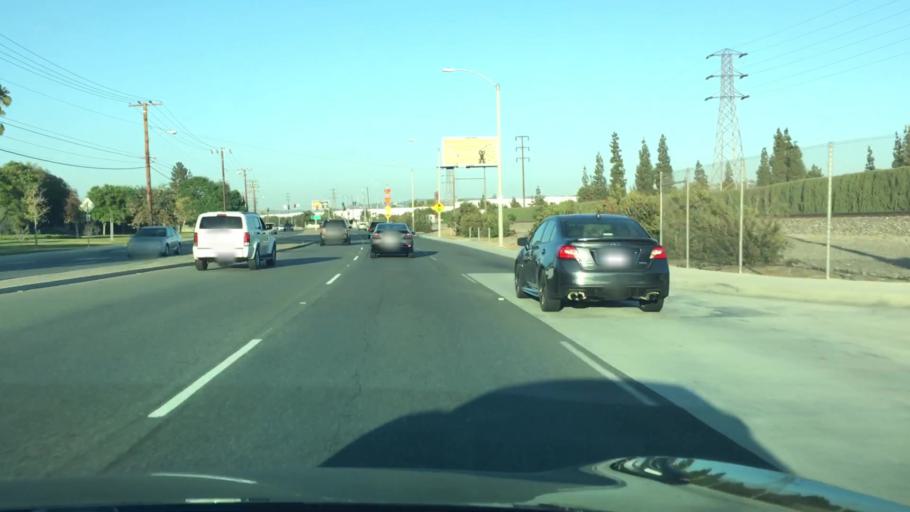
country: US
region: California
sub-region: Los Angeles County
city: Walnut
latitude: 34.0022
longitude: -117.8747
